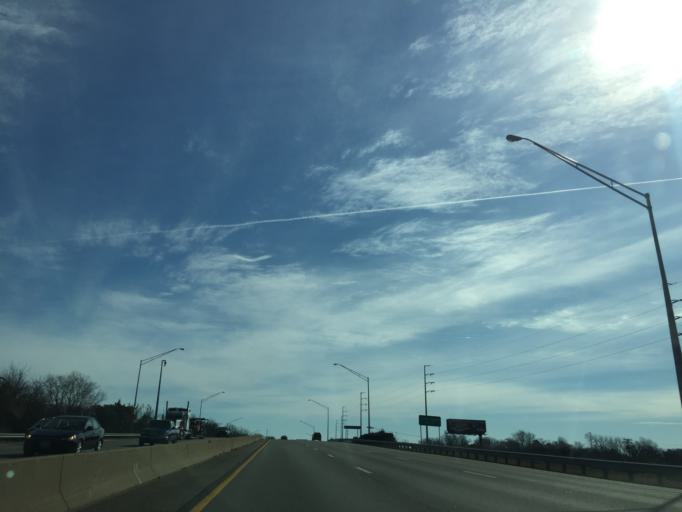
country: US
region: Virginia
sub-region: City of Hampton
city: Hampton
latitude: 37.0344
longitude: -76.3488
